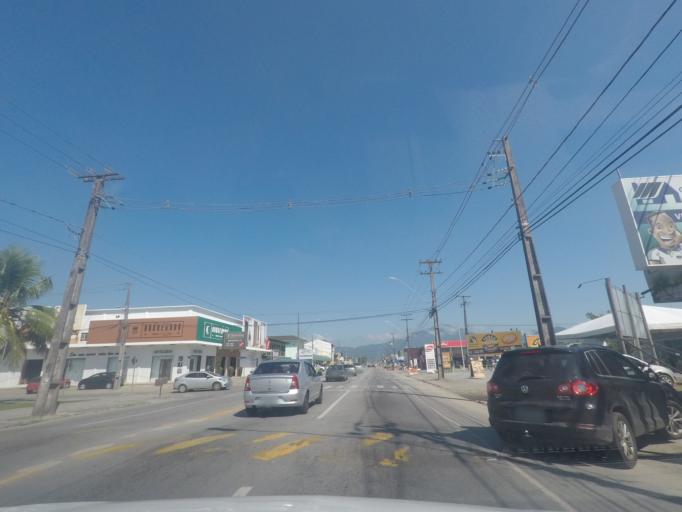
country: BR
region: Parana
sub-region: Paranagua
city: Paranagua
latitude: -25.5636
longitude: -48.5656
